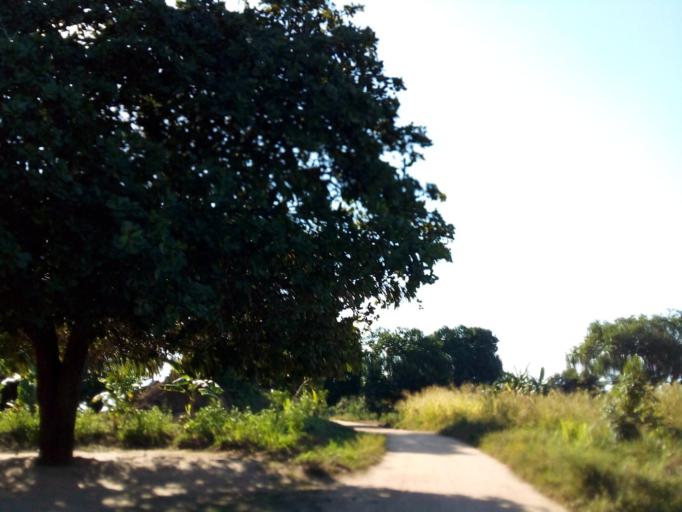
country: MZ
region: Zambezia
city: Quelimane
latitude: -17.5362
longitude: 36.6875
